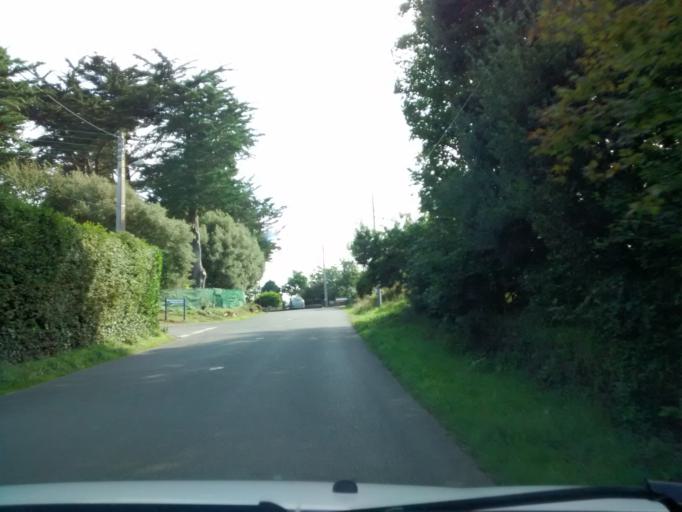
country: FR
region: Brittany
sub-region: Departement des Cotes-d'Armor
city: Penvenan
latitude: 48.8334
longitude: -3.3058
